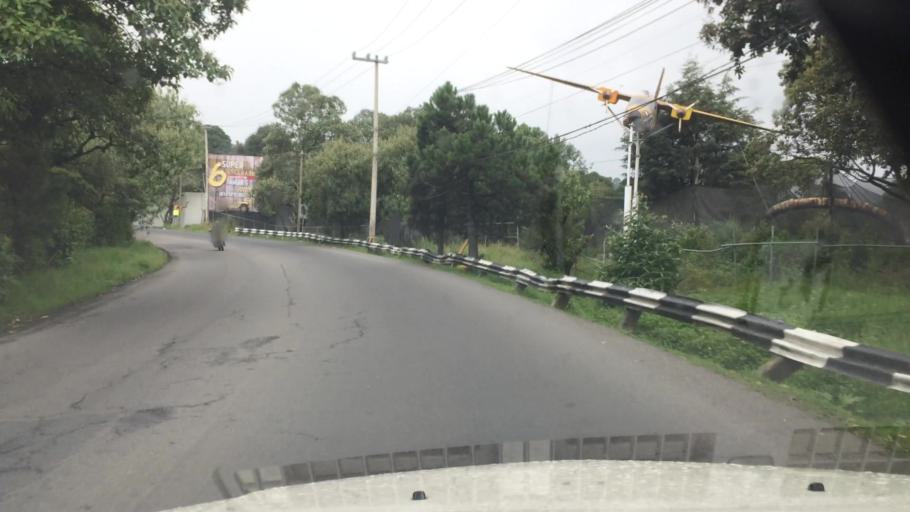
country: MX
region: Mexico City
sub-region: Tlalpan
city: Lomas de Tepemecatl
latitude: 19.2645
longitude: -99.2406
